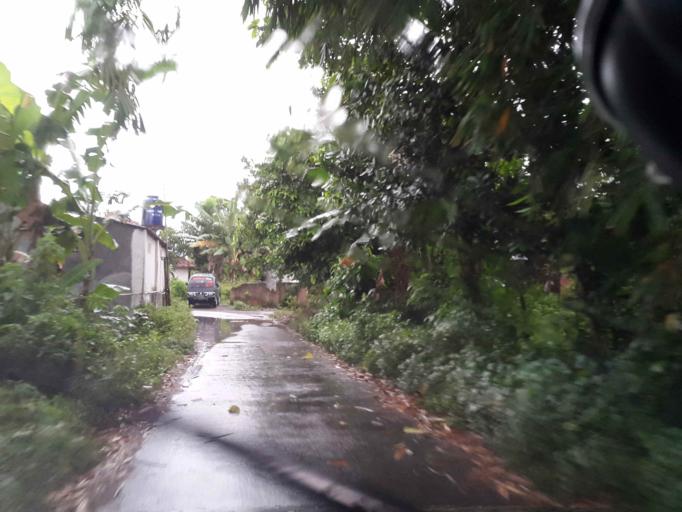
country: ID
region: West Nusa Tenggara
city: Karangkebon Timur
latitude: -8.6616
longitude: 116.1234
